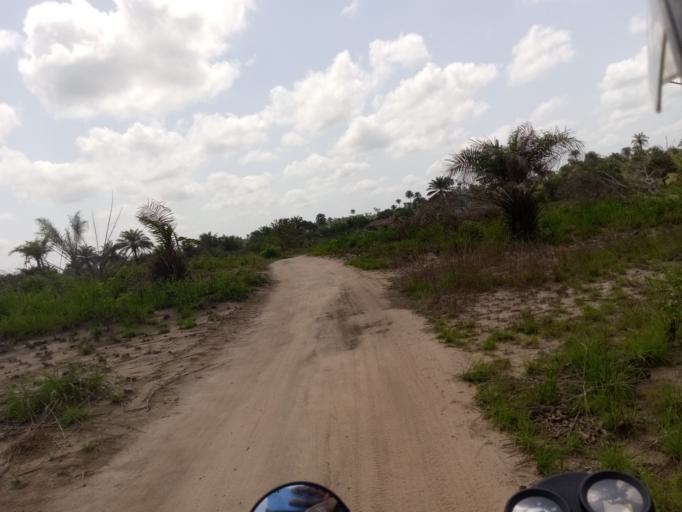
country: SL
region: Western Area
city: Waterloo
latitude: 8.3516
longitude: -13.0029
